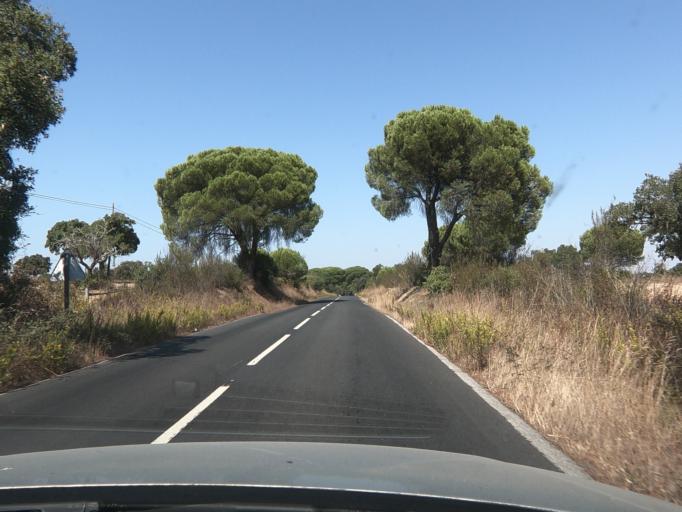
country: PT
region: Setubal
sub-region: Alcacer do Sal
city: Alcacer do Sal
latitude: 38.3353
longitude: -8.4419
